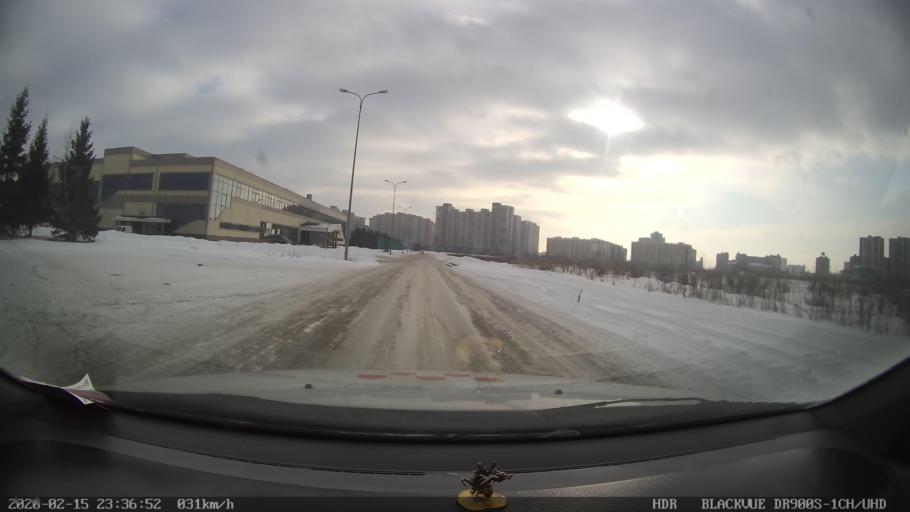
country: RU
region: Tatarstan
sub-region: Gorod Kazan'
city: Kazan
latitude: 55.7910
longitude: 49.1930
